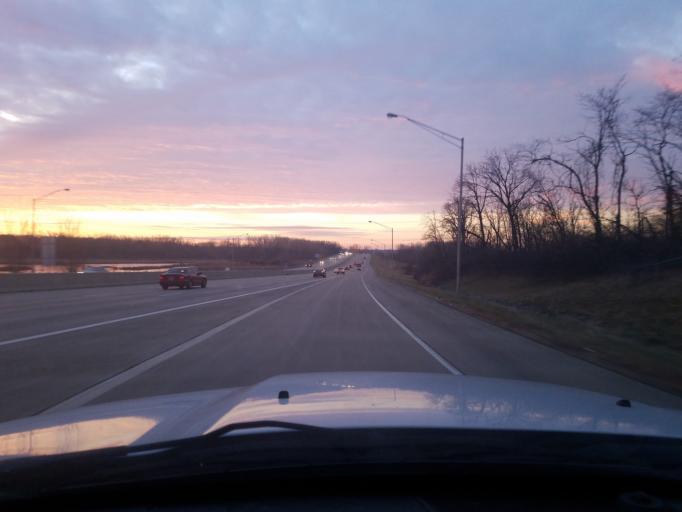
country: US
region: Indiana
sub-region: Huntington County
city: Roanoke
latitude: 41.0285
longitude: -85.2527
